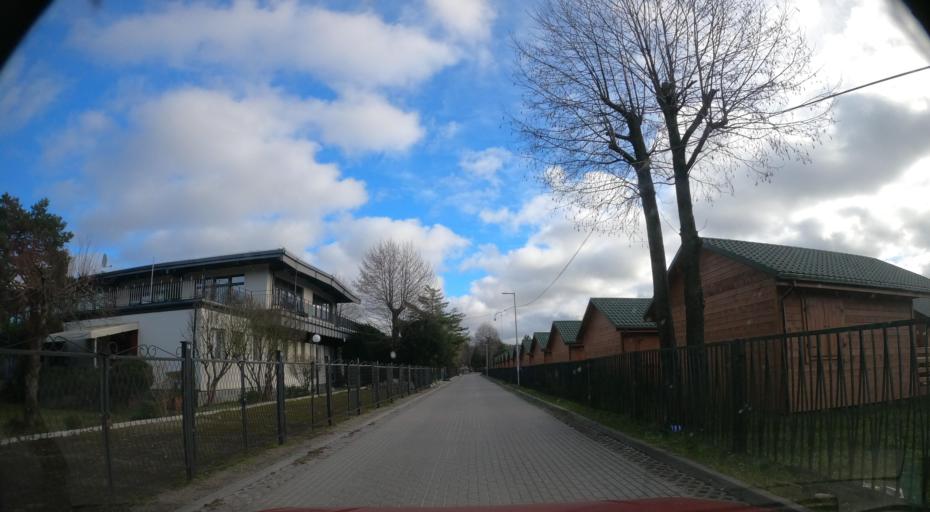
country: PL
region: West Pomeranian Voivodeship
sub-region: Powiat koszalinski
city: Sianow
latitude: 54.3139
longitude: 16.2062
